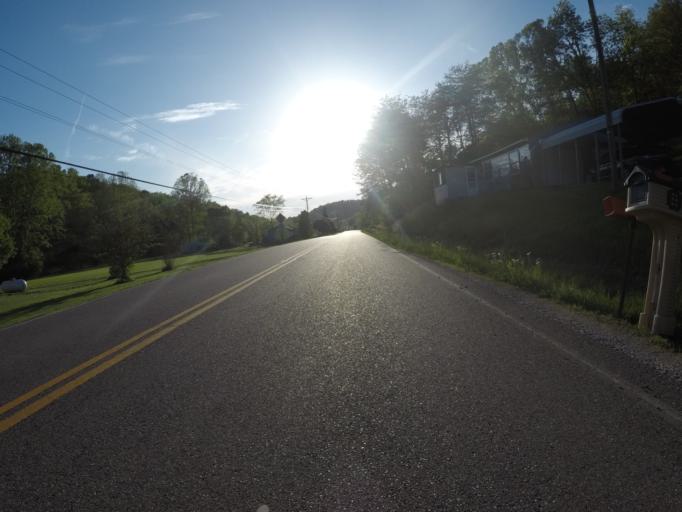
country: US
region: West Virginia
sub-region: Cabell County
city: Huntington
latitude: 38.5541
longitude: -82.4458
